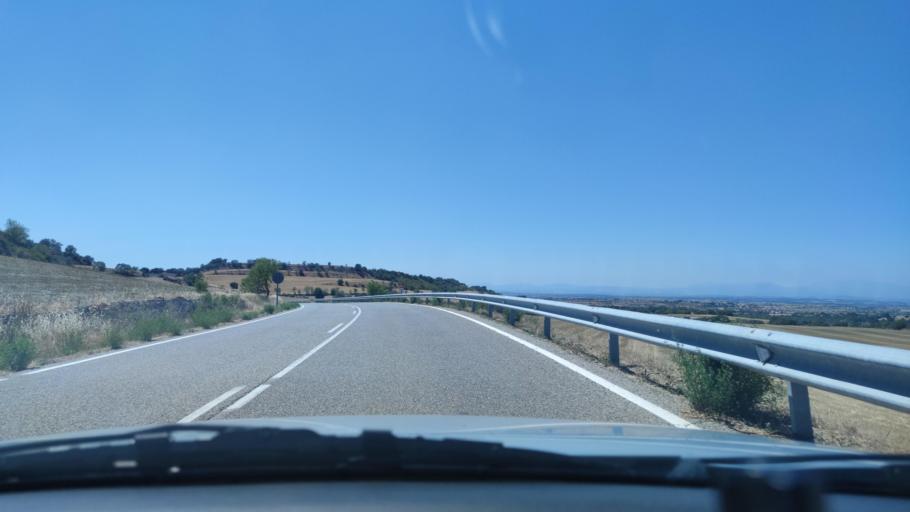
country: ES
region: Catalonia
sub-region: Provincia de Lleida
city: Ivorra
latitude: 41.7291
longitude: 1.3368
